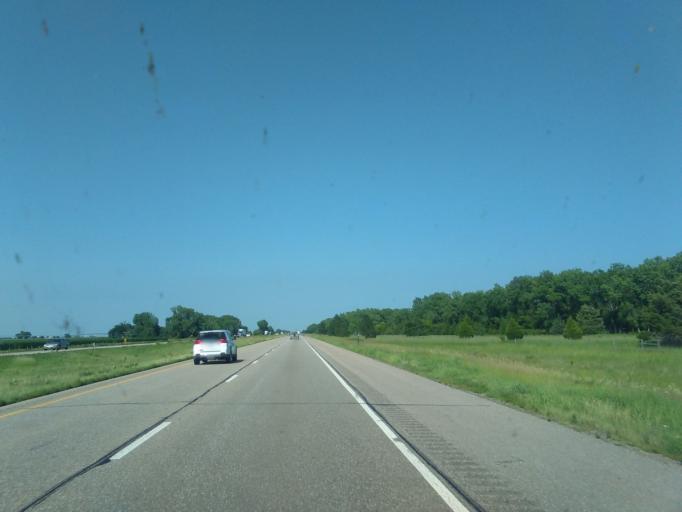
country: US
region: Nebraska
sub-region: Hall County
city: Wood River
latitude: 40.7733
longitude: -98.5541
